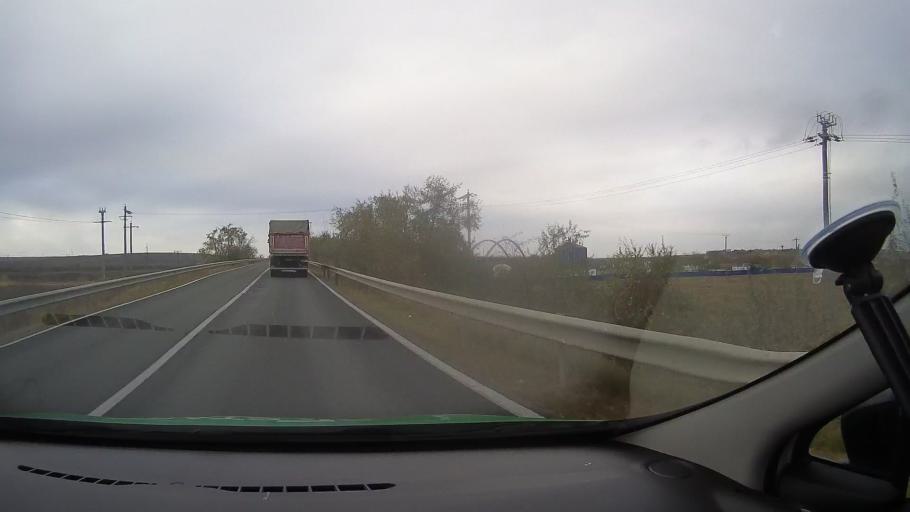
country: RO
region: Constanta
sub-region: Comuna Poarta Alba
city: Poarta Alba
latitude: 44.2143
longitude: 28.3924
